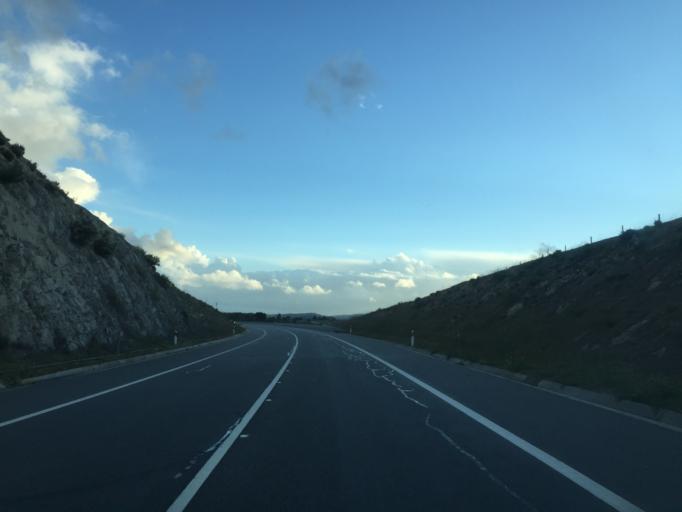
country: PT
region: Guarda
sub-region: Meda
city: Meda
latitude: 40.9330
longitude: -7.1958
